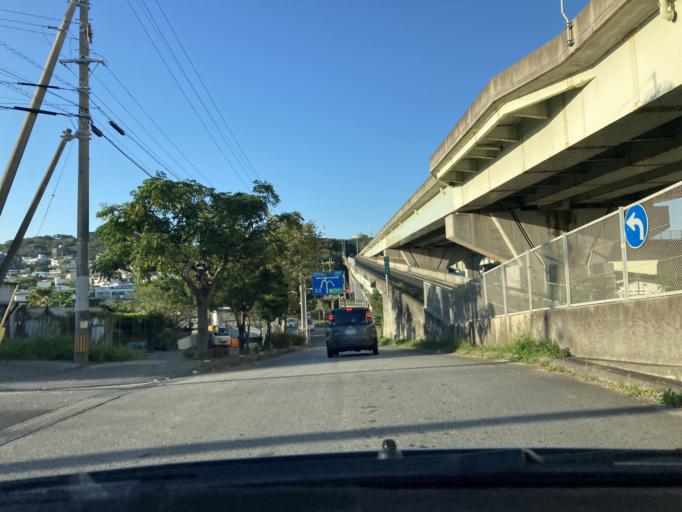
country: JP
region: Okinawa
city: Naha-shi
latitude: 26.2043
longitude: 127.7383
